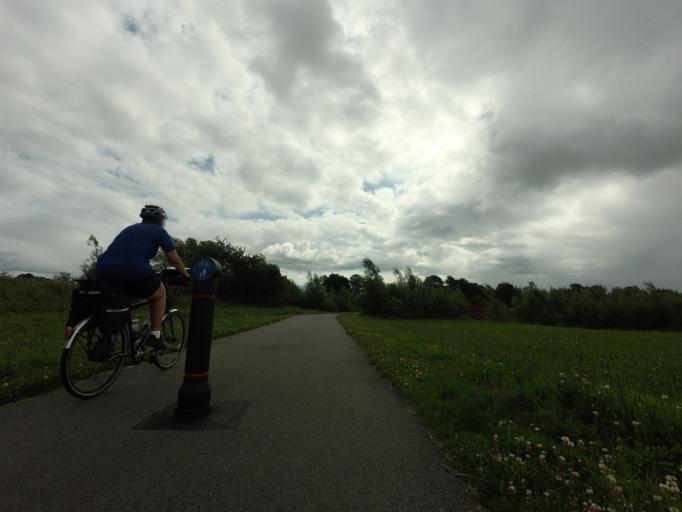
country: GB
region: Scotland
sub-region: Moray
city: Lhanbryd
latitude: 57.6432
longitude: -3.2652
